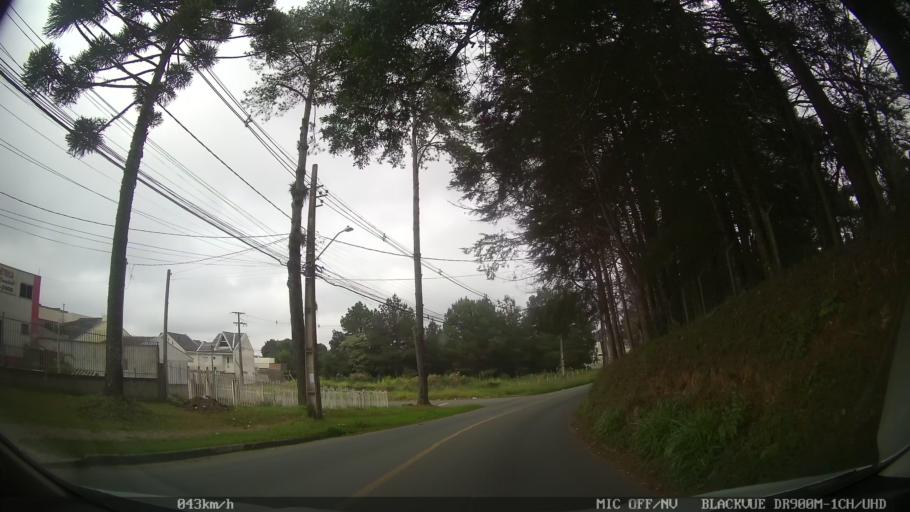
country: BR
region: Parana
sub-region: Almirante Tamandare
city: Almirante Tamandare
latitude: -25.3585
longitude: -49.2721
